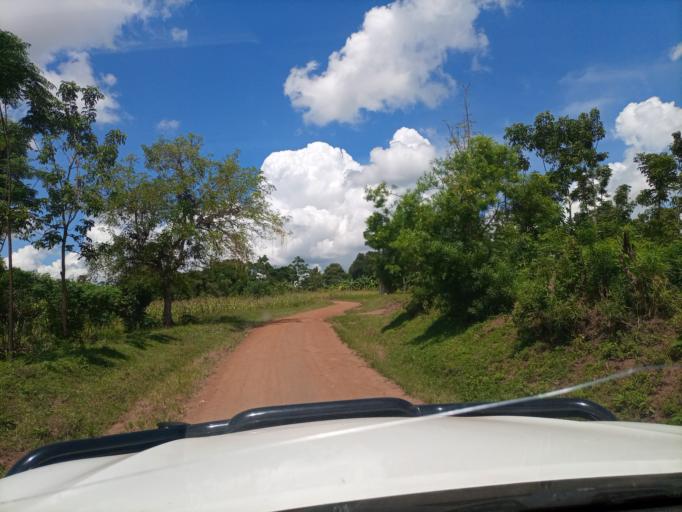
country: UG
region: Eastern Region
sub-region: Tororo District
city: Tororo
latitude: 0.6963
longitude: 34.0117
